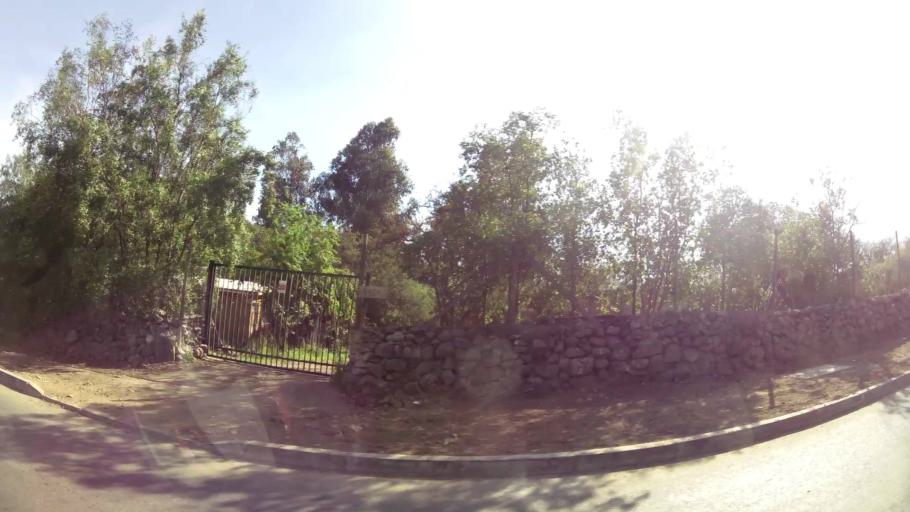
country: CL
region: Santiago Metropolitan
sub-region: Provincia de Santiago
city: Villa Presidente Frei, Nunoa, Santiago, Chile
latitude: -33.4927
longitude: -70.5376
